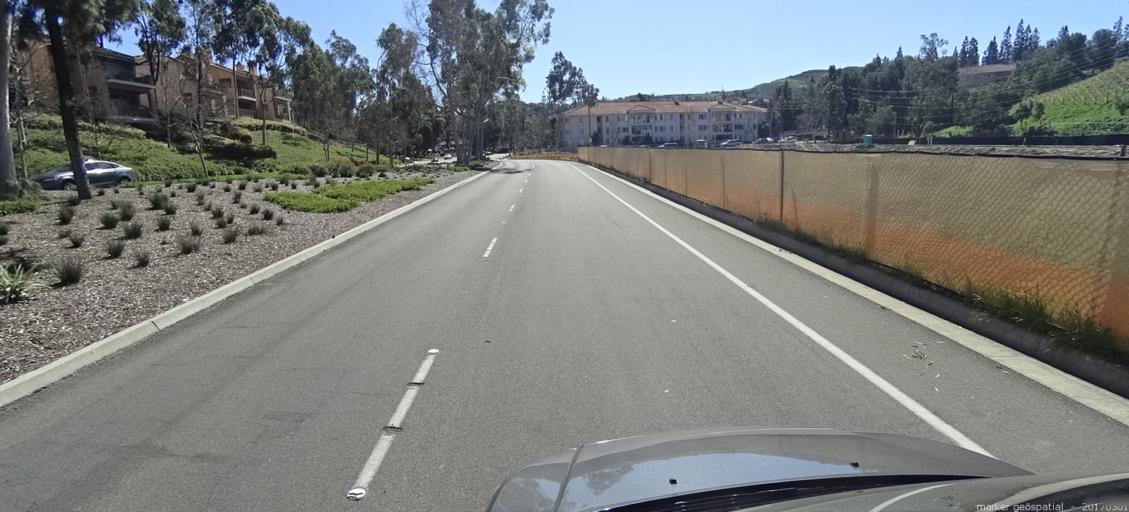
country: US
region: California
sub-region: Orange County
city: Villa Park
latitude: 33.8473
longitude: -117.7783
